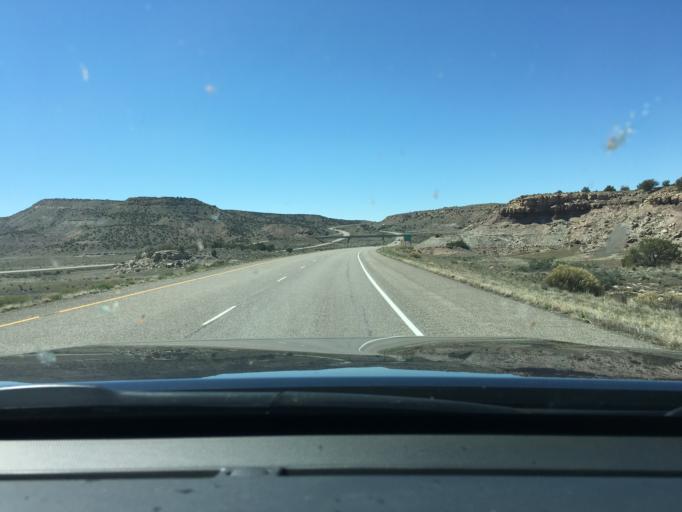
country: US
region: Colorado
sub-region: Mesa County
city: Loma
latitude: 39.1929
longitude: -109.0087
